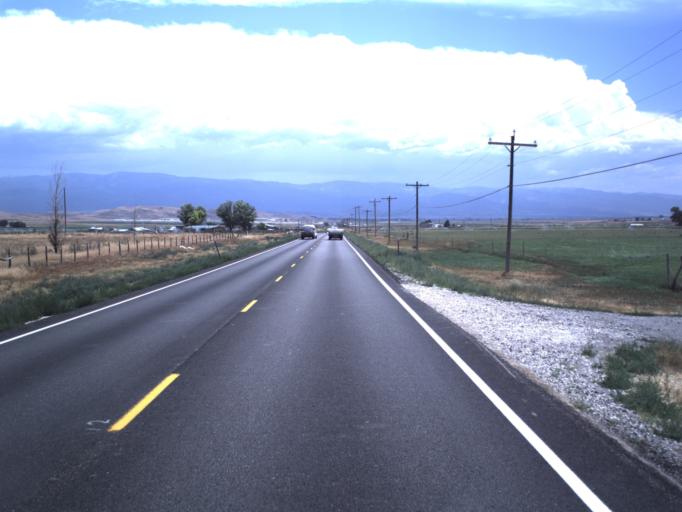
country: US
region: Utah
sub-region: Sanpete County
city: Fountain Green
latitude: 39.6031
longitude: -111.6231
